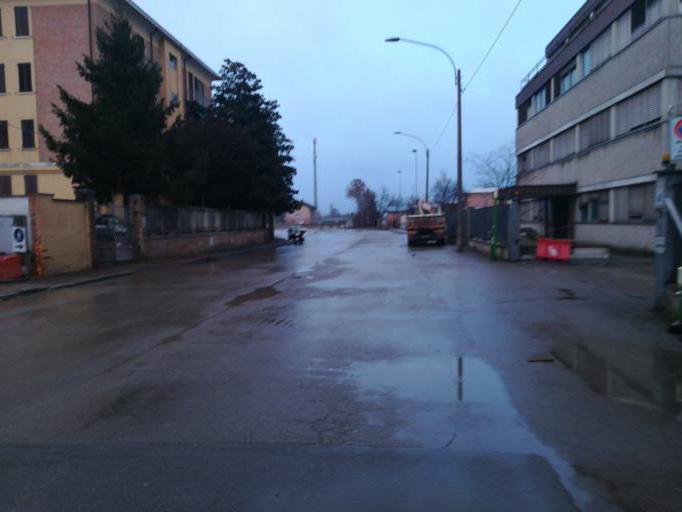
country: IT
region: Emilia-Romagna
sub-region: Provincia di Bologna
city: Progresso
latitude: 44.5504
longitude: 11.3542
